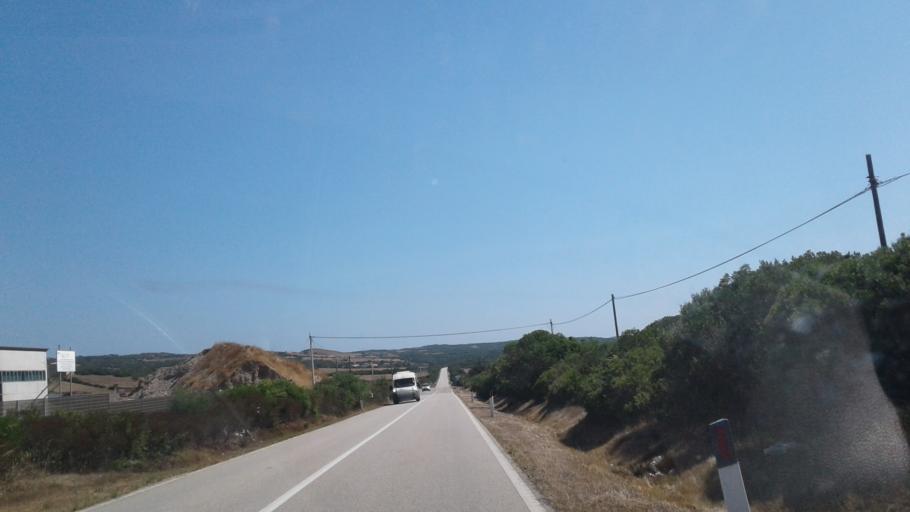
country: IT
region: Sardinia
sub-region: Provincia di Olbia-Tempio
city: Luogosanto
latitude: 41.1171
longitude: 9.2662
